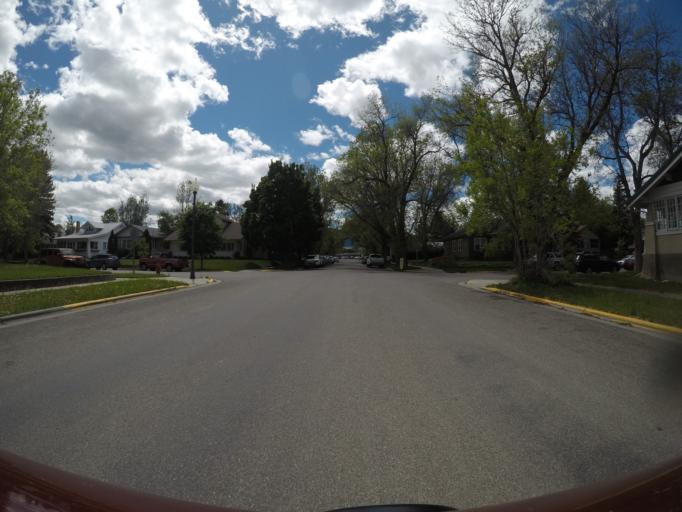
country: US
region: Montana
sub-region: Park County
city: Livingston
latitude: 45.6572
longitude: -110.5678
